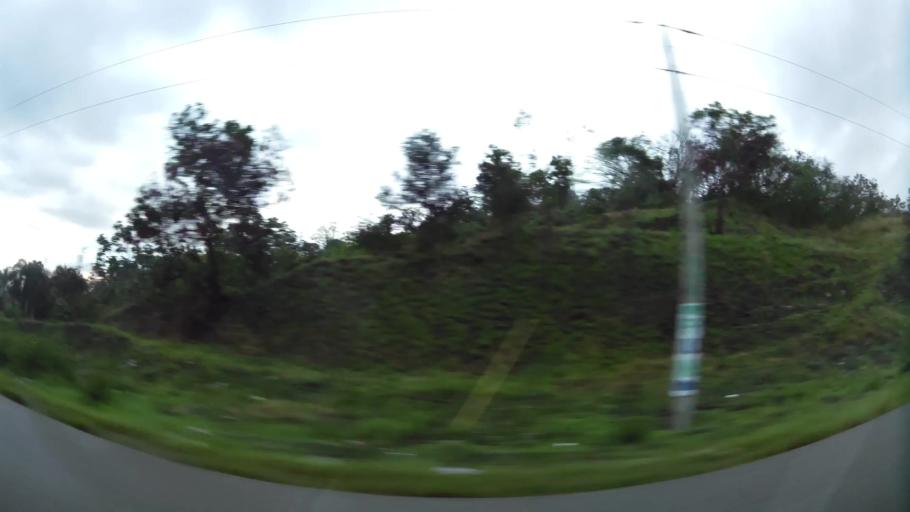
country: DO
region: San Cristobal
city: Villa Altagracia
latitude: 18.6062
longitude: -70.1418
